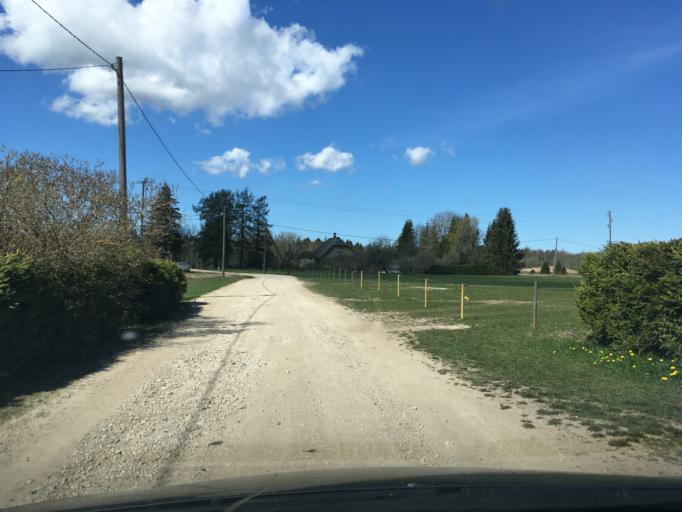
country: EE
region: Harju
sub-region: Raasiku vald
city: Raasiku
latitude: 59.2162
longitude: 25.1608
